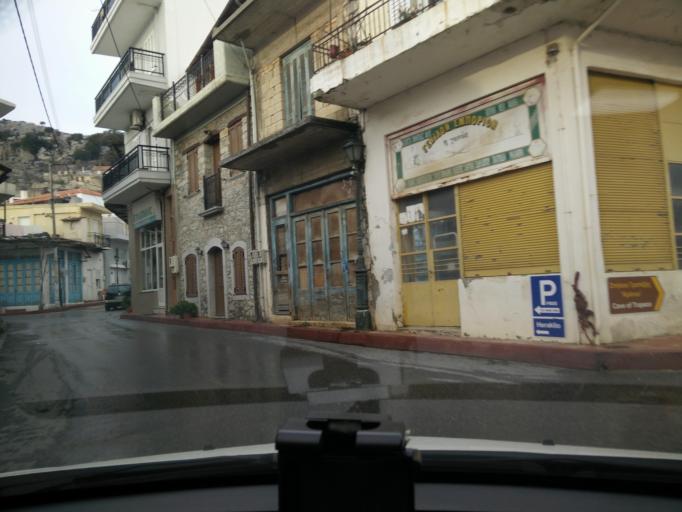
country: GR
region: Crete
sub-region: Nomos Irakleiou
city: Malia
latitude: 35.1986
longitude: 25.4889
